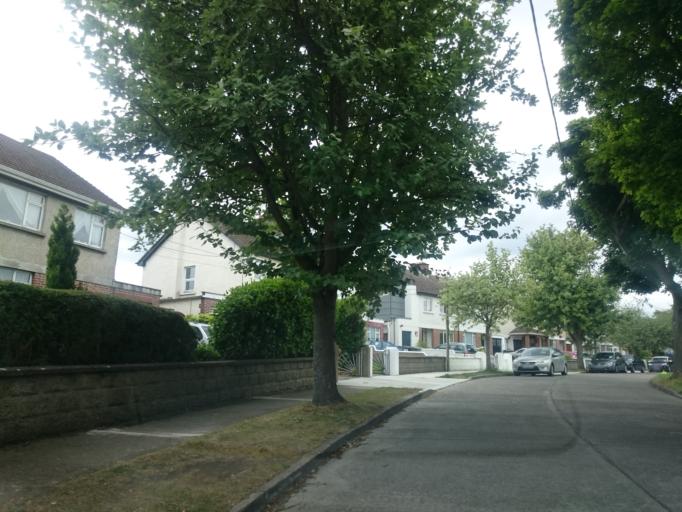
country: IE
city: Booterstown
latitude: 53.2871
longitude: -6.2013
